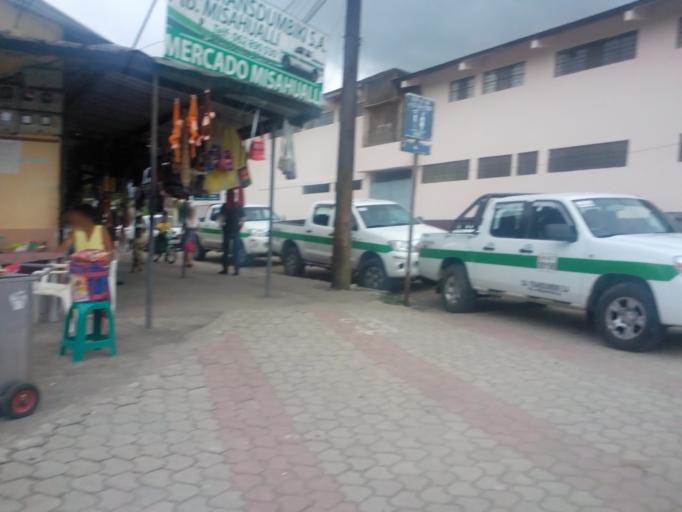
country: EC
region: Napo
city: Tena
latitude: -1.0357
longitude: -77.6670
